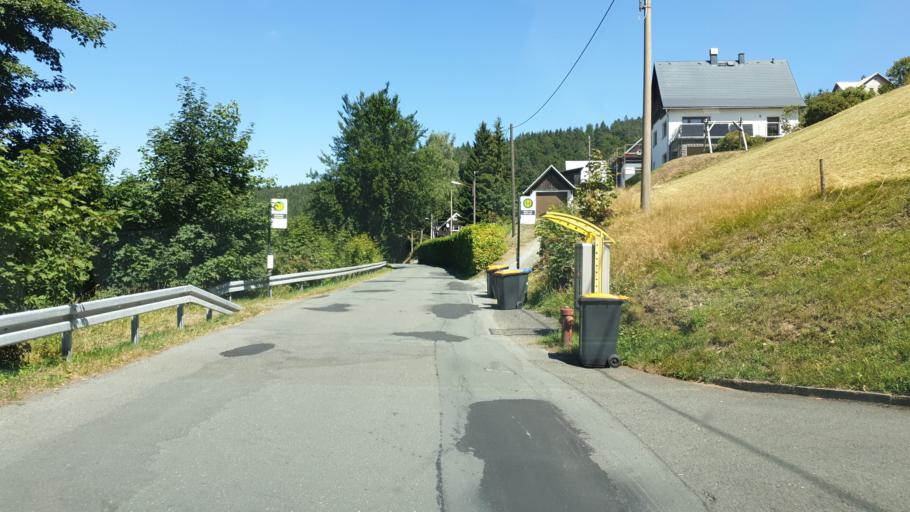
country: DE
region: Saxony
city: Klingenthal
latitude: 50.3880
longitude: 12.4955
